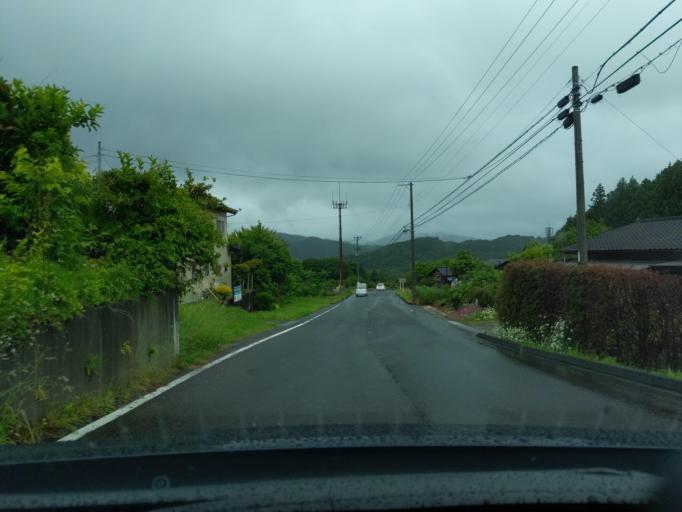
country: JP
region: Fukushima
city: Hobaramachi
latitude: 37.6683
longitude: 140.6371
